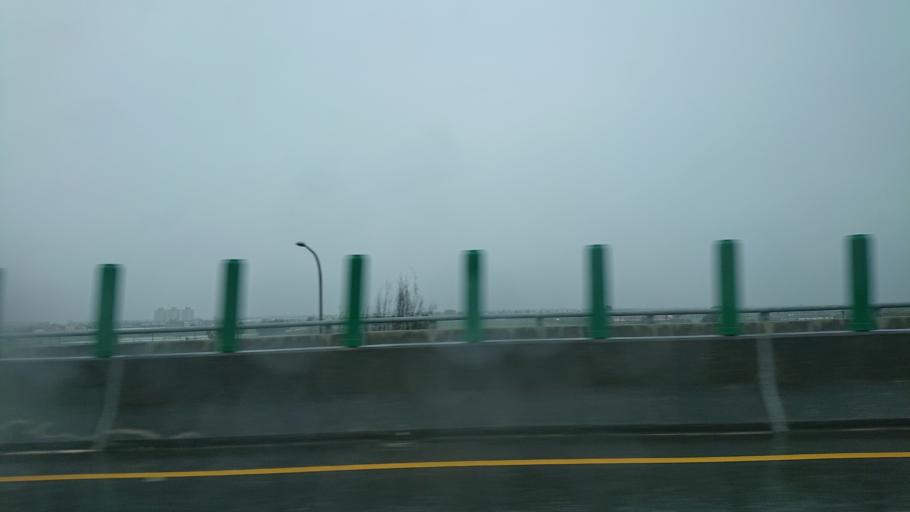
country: TW
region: Taiwan
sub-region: Yunlin
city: Douliu
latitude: 23.7892
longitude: 120.2762
